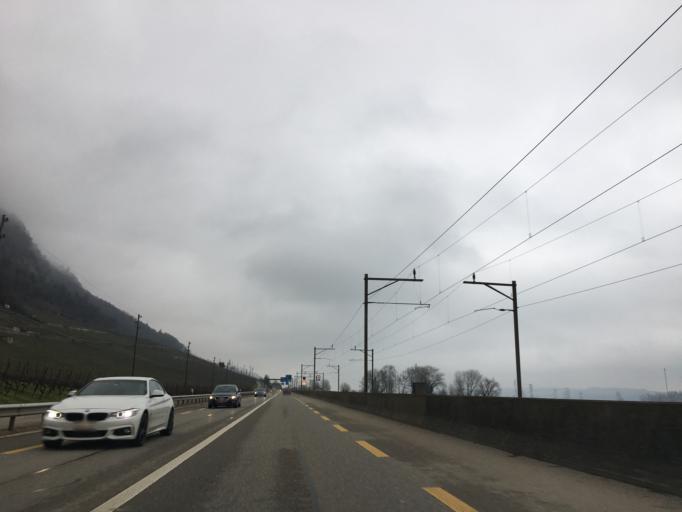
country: CH
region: Bern
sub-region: Jura bernois
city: La Neuveville
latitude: 47.0768
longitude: 7.1173
